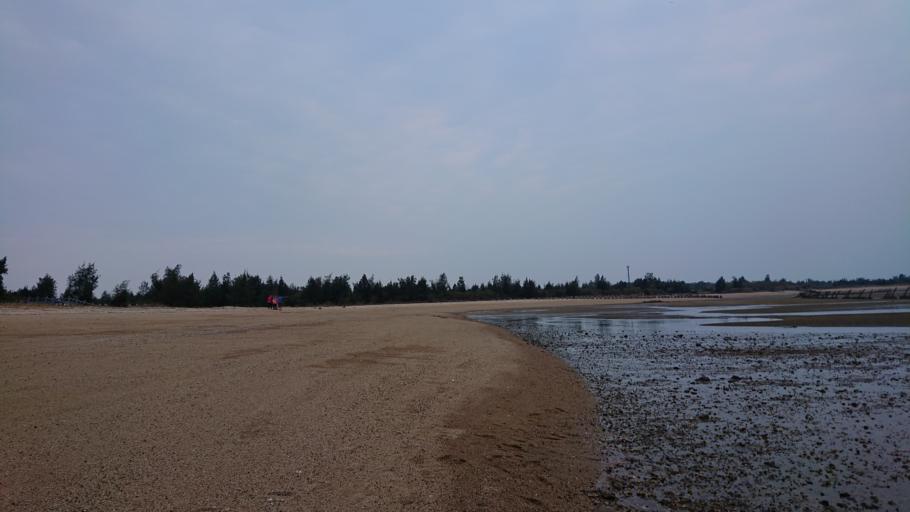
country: TW
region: Fukien
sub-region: Kinmen
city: Jincheng
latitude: 24.4292
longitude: 118.2264
